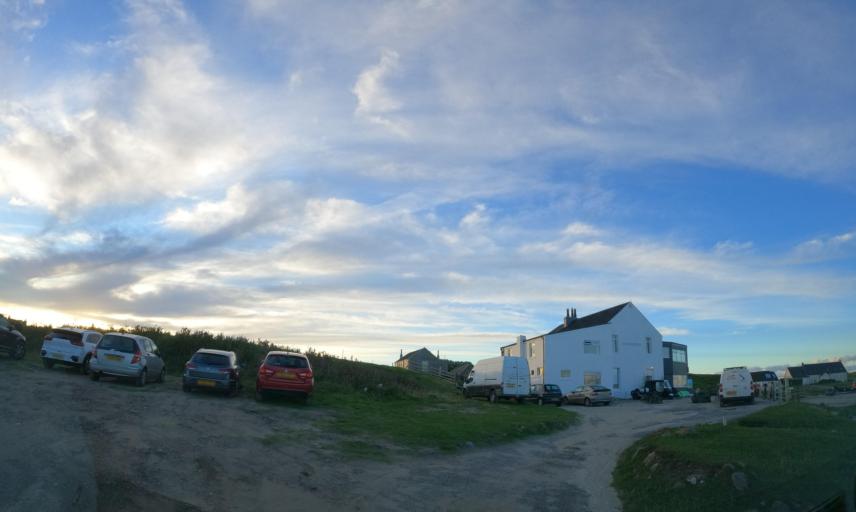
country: GB
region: Scotland
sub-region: Eilean Siar
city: Barra
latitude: 56.5011
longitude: -6.8062
